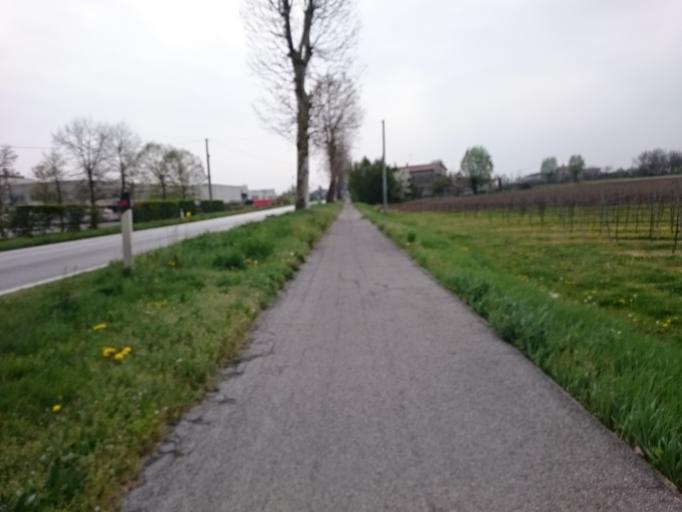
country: IT
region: Veneto
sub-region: Provincia di Padova
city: Bagnoli di Sopra
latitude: 45.2022
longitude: 11.8837
